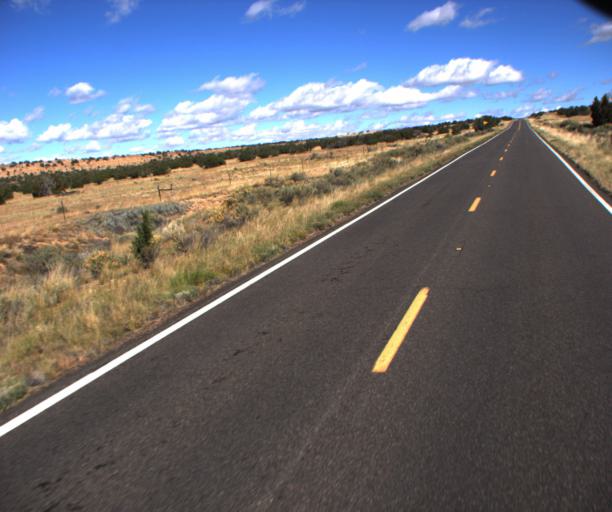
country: US
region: Arizona
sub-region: Apache County
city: Saint Johns
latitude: 34.8128
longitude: -109.2377
